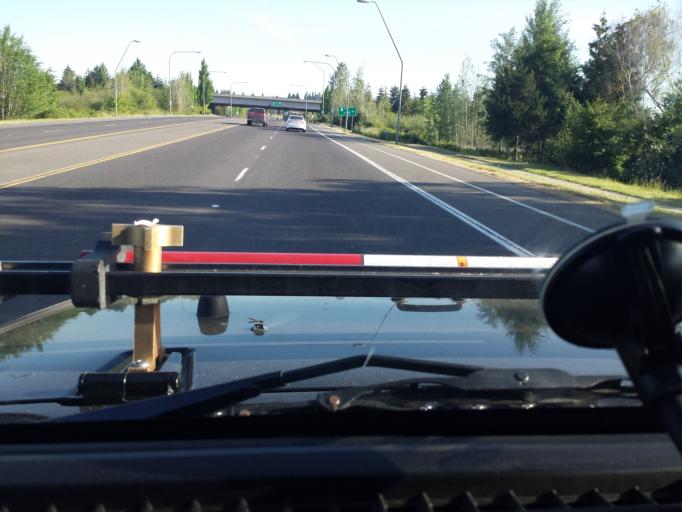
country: US
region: Washington
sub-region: Clark County
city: Walnut Grove
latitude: 45.6461
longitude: -122.6007
